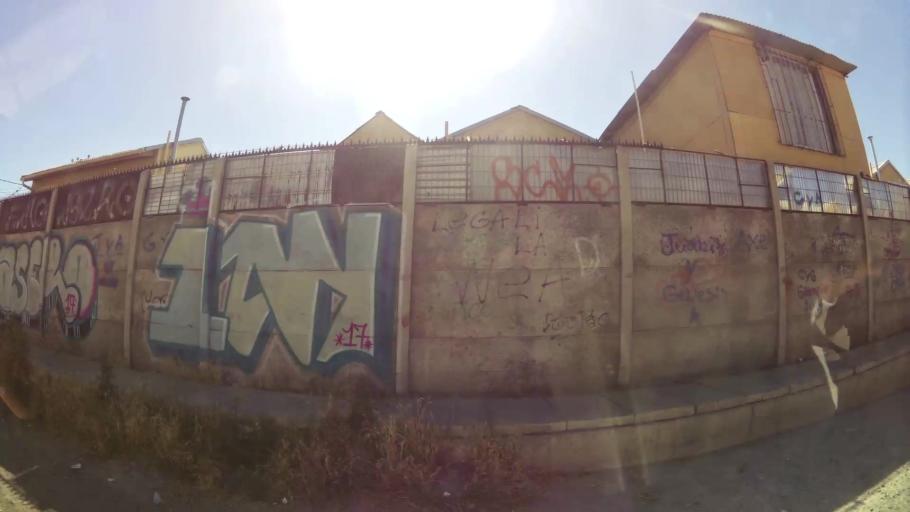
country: CL
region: Santiago Metropolitan
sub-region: Provincia de Maipo
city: San Bernardo
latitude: -33.5873
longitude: -70.6730
